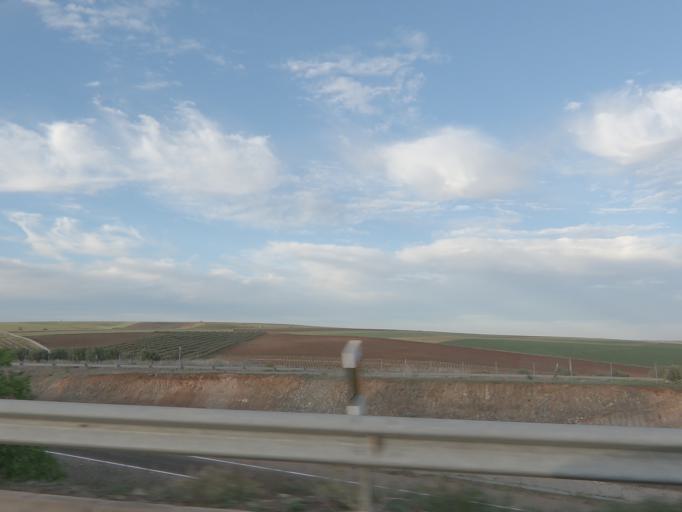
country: ES
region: Extremadura
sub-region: Provincia de Badajoz
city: Merida
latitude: 38.9482
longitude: -6.3416
